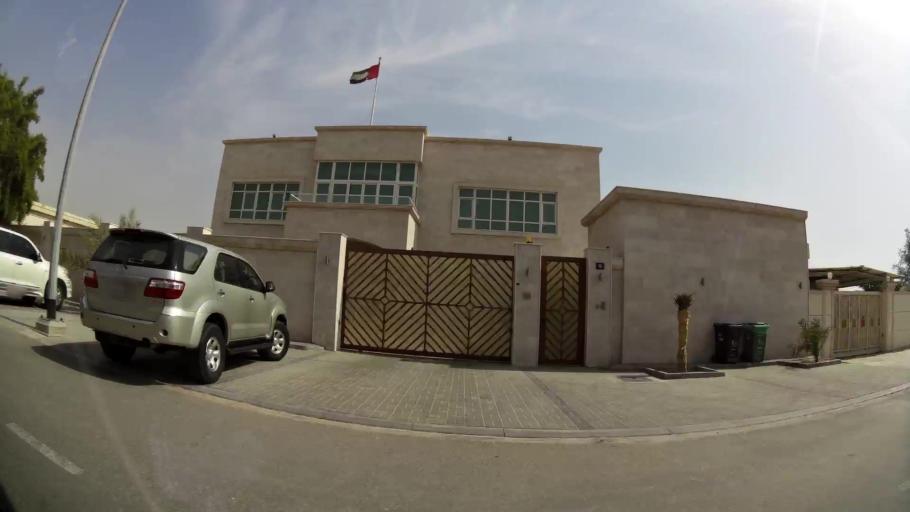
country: AE
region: Ash Shariqah
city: Sharjah
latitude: 25.2477
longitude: 55.4344
